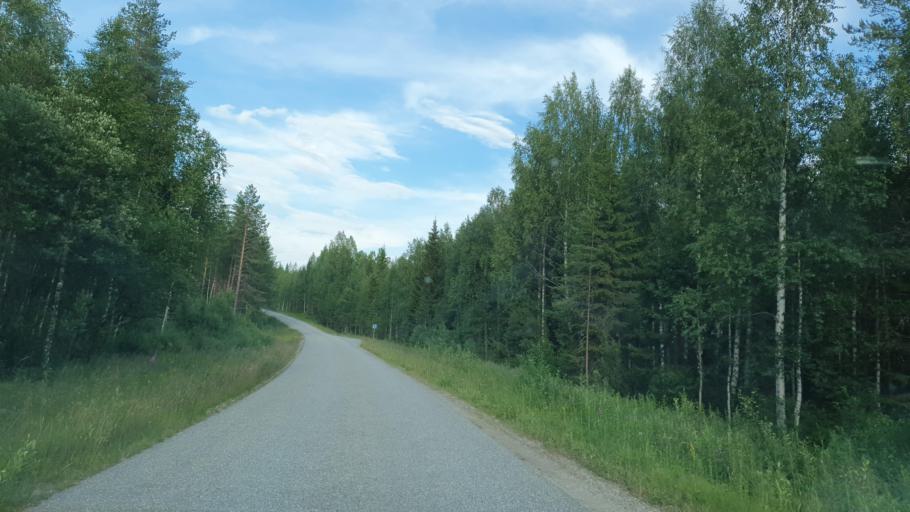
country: FI
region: Kainuu
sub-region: Kehys-Kainuu
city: Kuhmo
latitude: 64.2759
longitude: 29.4407
